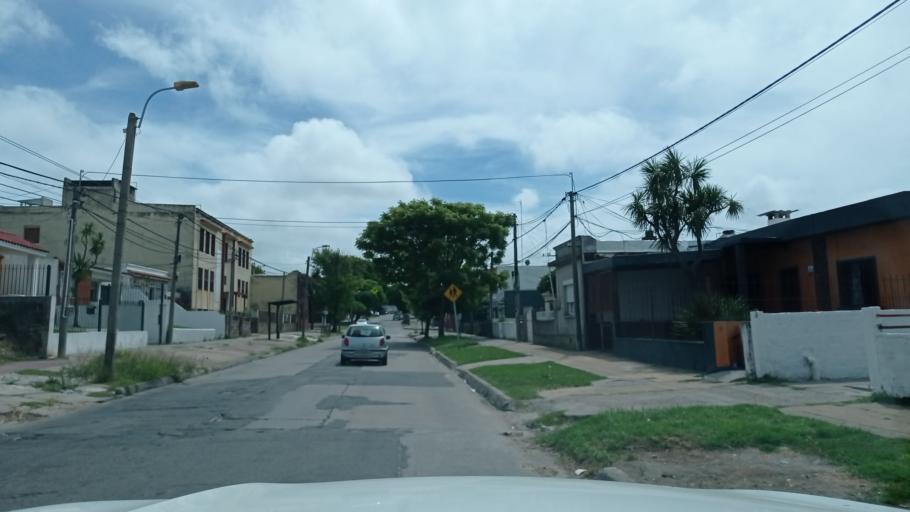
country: UY
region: Montevideo
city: Montevideo
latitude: -34.8655
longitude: -56.1297
